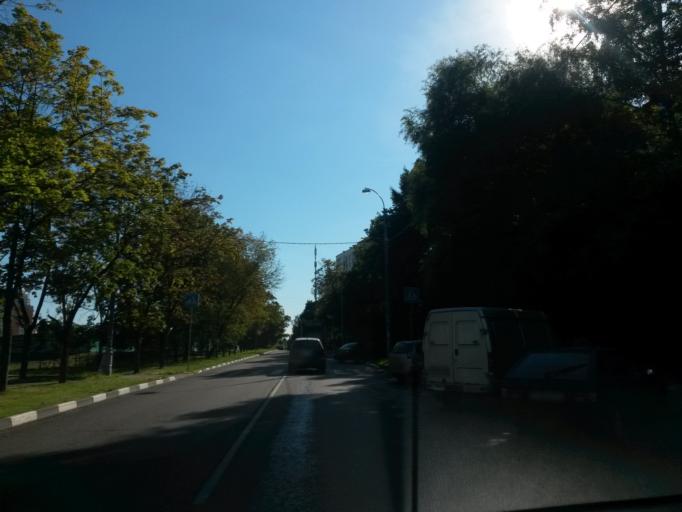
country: RU
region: Moscow
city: Kotlovka
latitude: 55.6596
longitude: 37.5873
